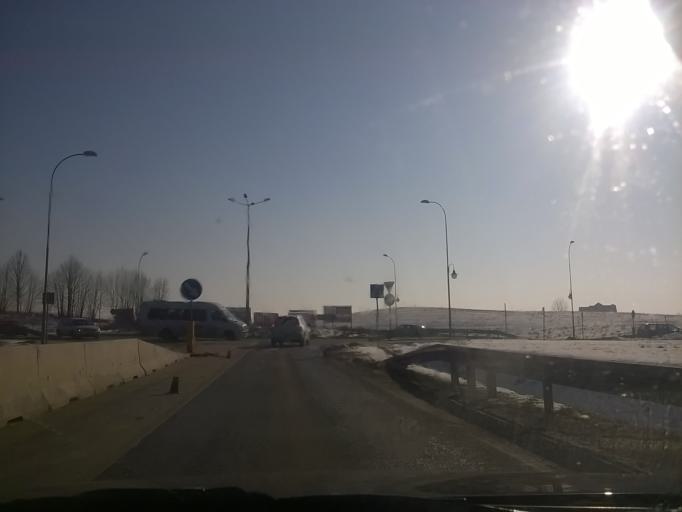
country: PL
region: Warmian-Masurian Voivodeship
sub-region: Powiat mragowski
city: Mragowo
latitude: 53.8608
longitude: 21.2794
